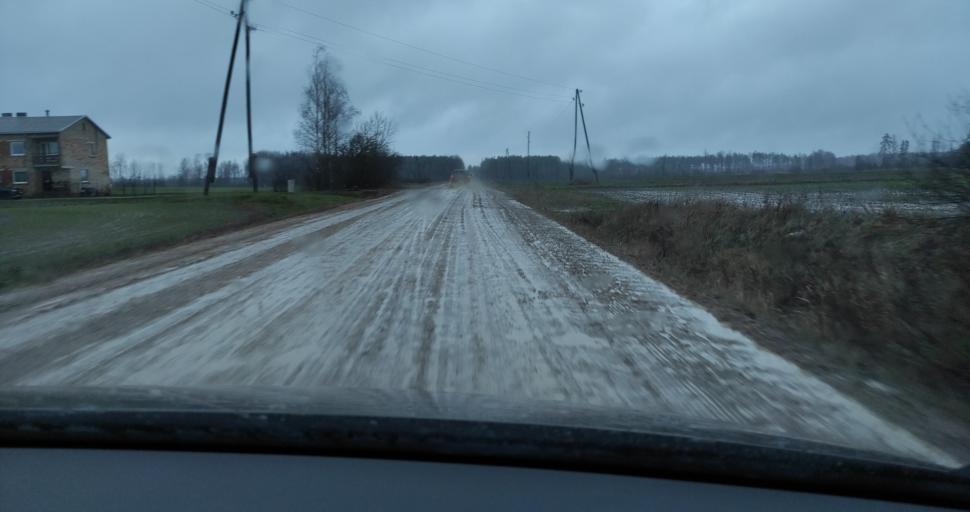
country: LV
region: Skrunda
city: Skrunda
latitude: 56.6791
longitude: 22.2205
